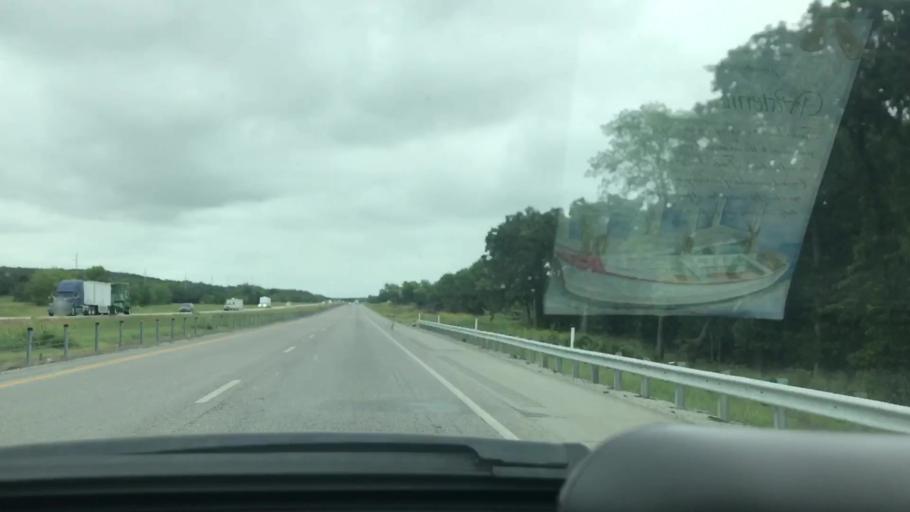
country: US
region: Oklahoma
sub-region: Coal County
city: Coalgate
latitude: 34.6313
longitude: -95.9565
